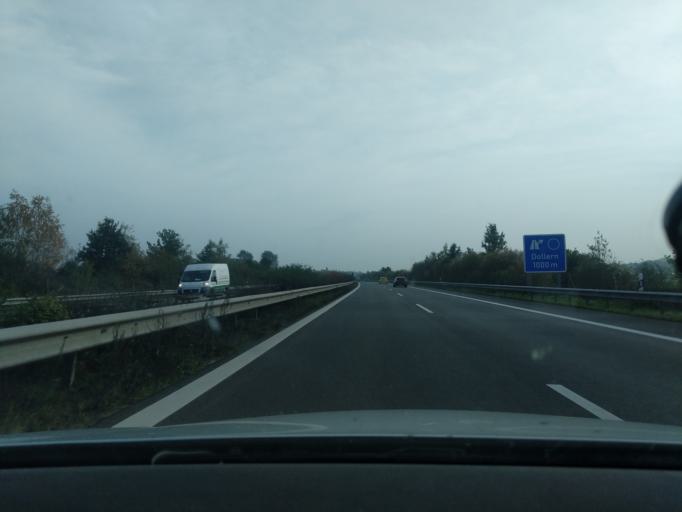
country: DE
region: Lower Saxony
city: Dollern
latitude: 53.5540
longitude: 9.5610
